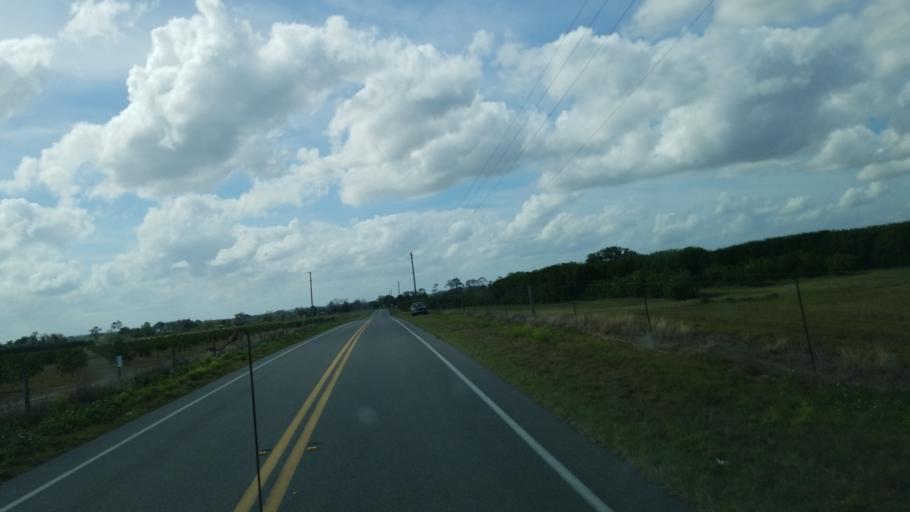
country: US
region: Florida
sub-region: Polk County
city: Babson Park
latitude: 27.9252
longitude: -81.4774
